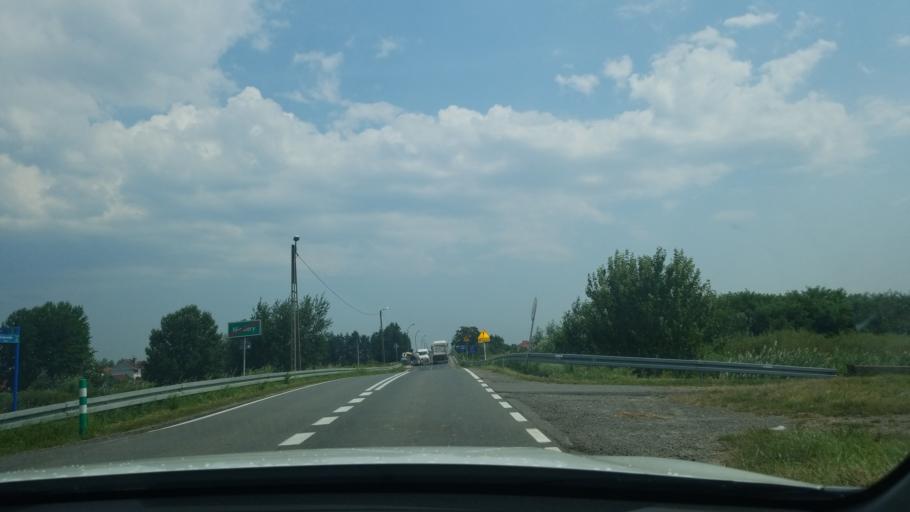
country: PL
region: Lesser Poland Voivodeship
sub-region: Powiat bochenski
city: Dziewin
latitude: 50.1183
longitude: 20.5085
